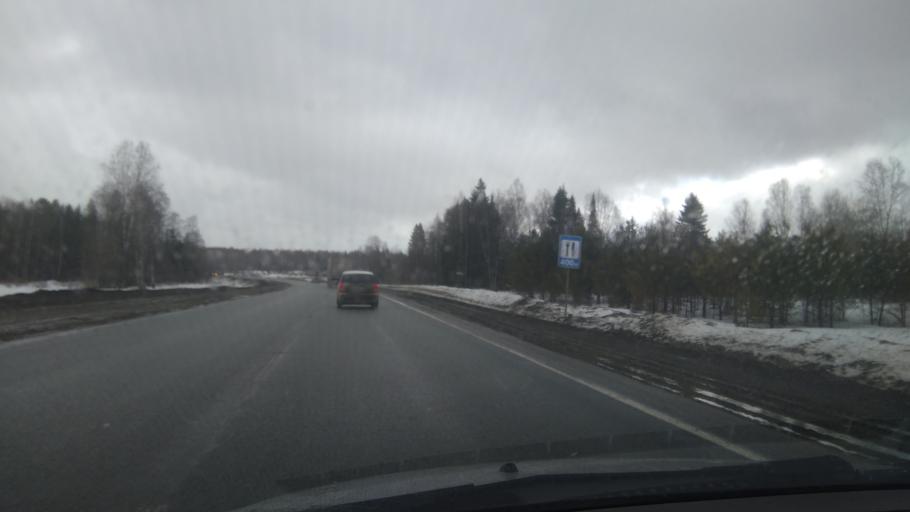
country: RU
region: Sverdlovsk
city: Ufimskiy
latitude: 56.7837
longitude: 58.3956
